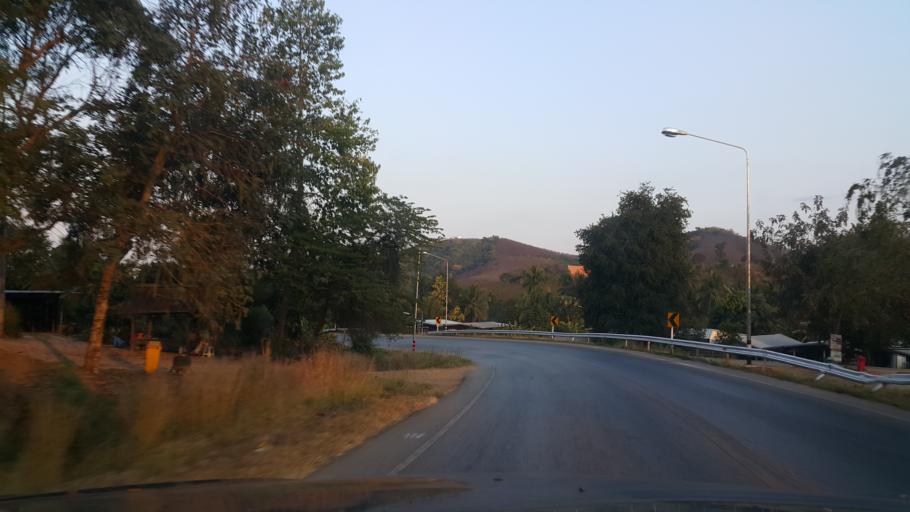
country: TH
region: Loei
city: Loei
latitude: 17.4816
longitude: 101.6265
